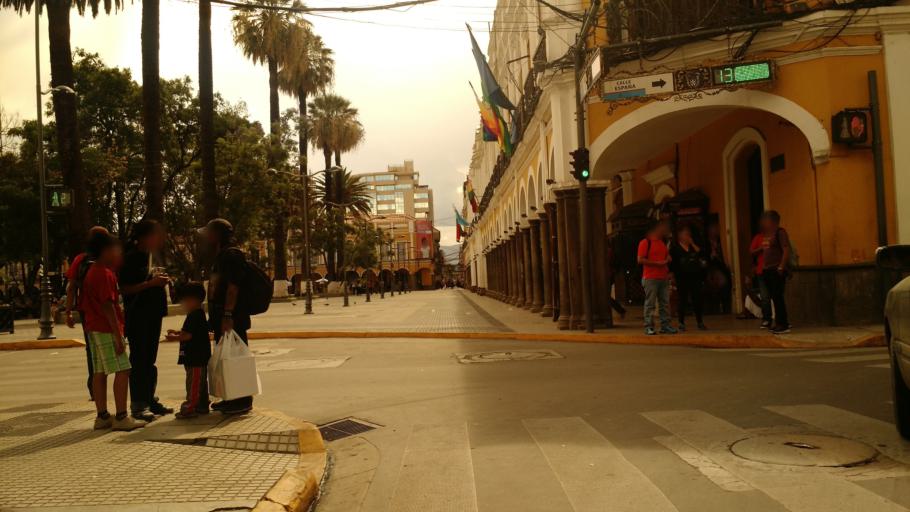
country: BO
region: Cochabamba
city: Cochabamba
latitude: -17.3932
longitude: -66.1564
